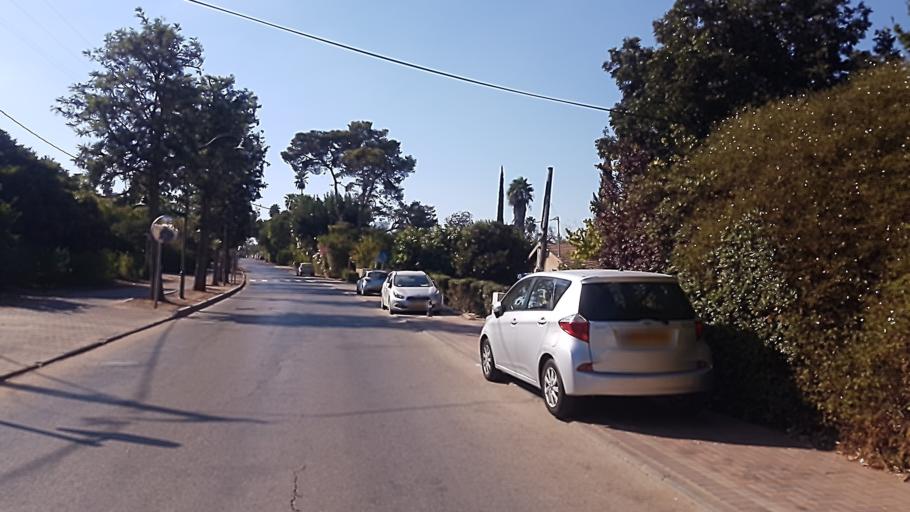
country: IL
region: Central District
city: Ra'anana
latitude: 32.2109
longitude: 34.8971
